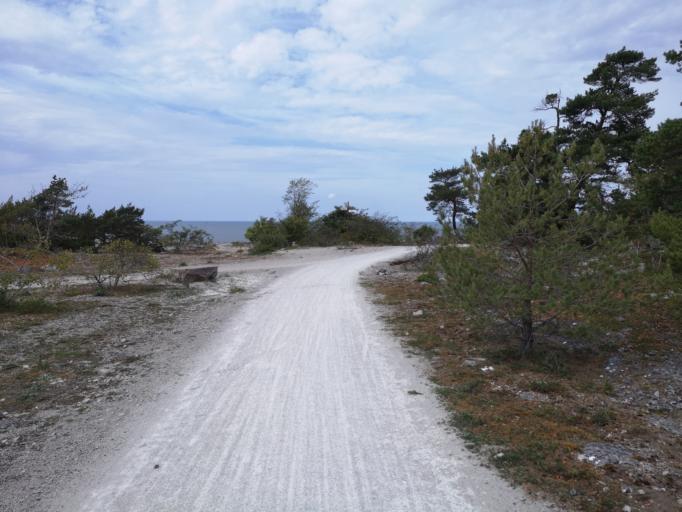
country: SE
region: Gotland
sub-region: Gotland
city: Vibble
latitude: 57.6152
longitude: 18.2594
